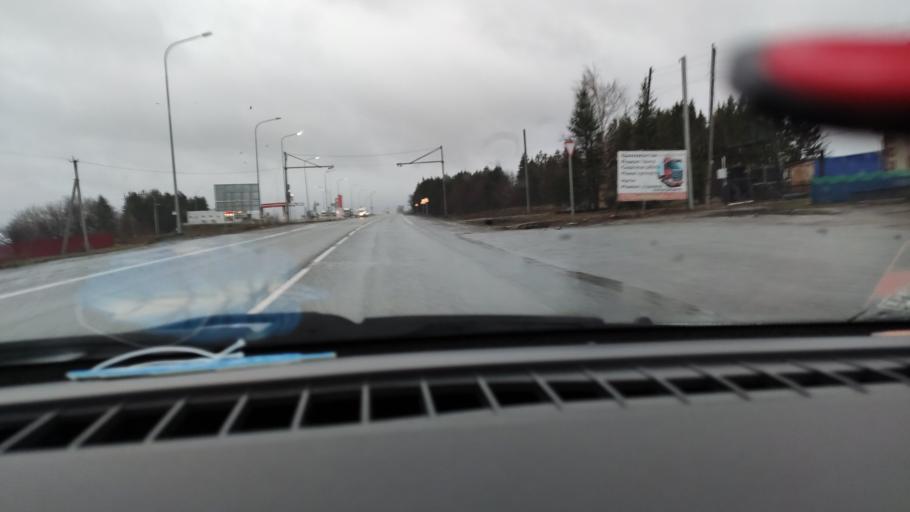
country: RU
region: Tatarstan
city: Mendeleyevsk
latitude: 56.0269
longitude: 52.3692
